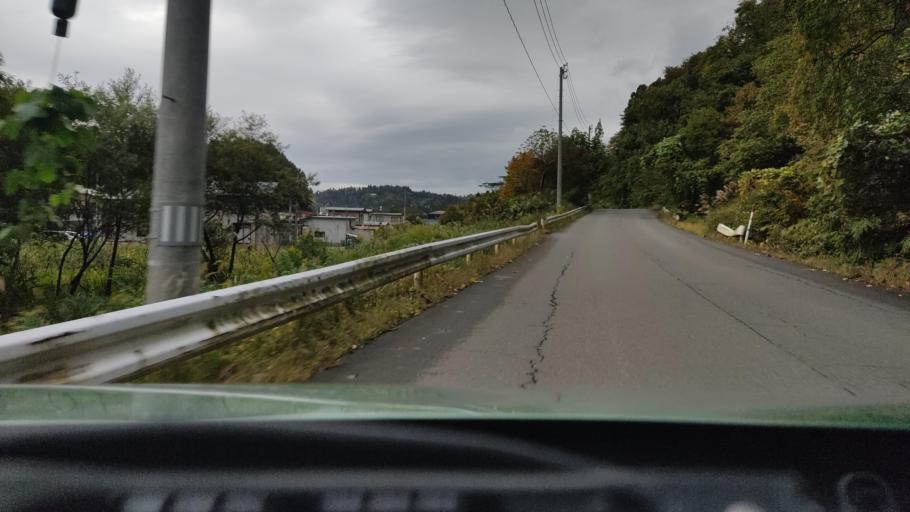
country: JP
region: Akita
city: Yokotemachi
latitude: 39.3003
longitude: 140.5742
